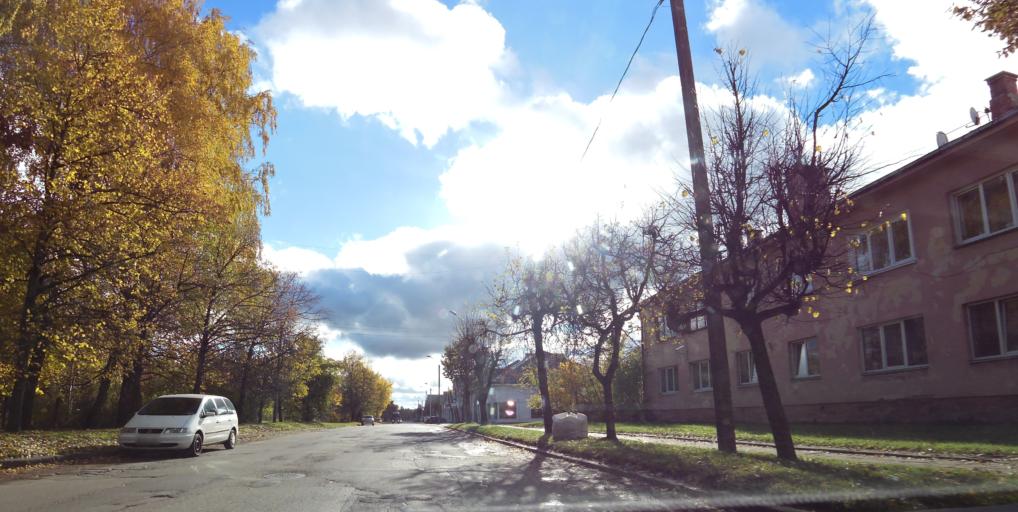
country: LT
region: Vilnius County
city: Naujamiestis
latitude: 54.6419
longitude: 25.2742
